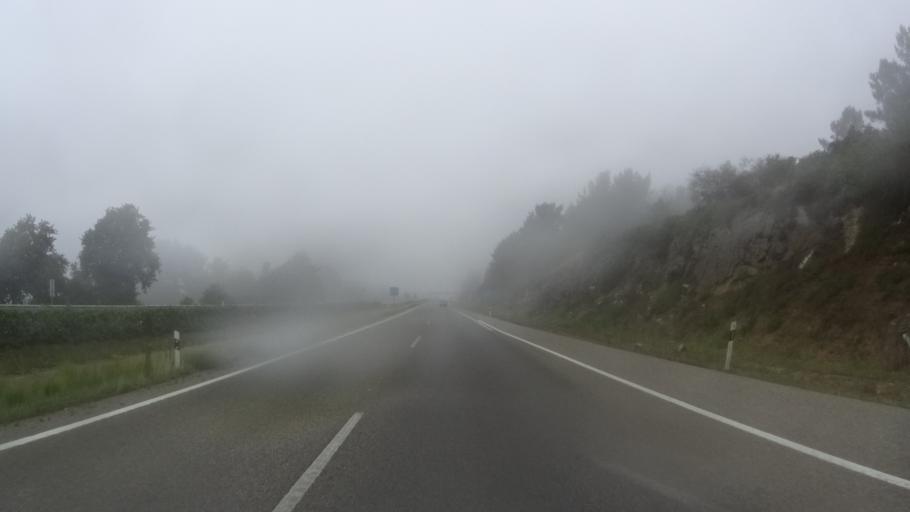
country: ES
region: Galicia
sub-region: Provincia de Lugo
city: Guitiriz
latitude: 43.1858
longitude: -7.8324
